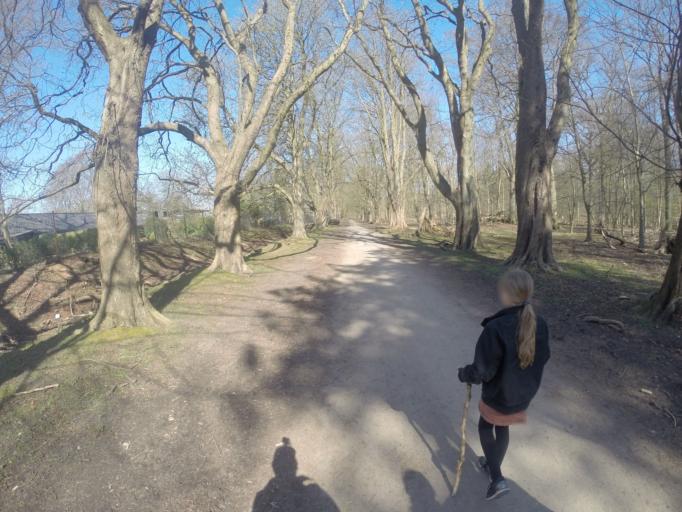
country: DK
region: Capital Region
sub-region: Lyngby-Tarbaek Kommune
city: Kongens Lyngby
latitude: 55.7815
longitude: 12.5445
